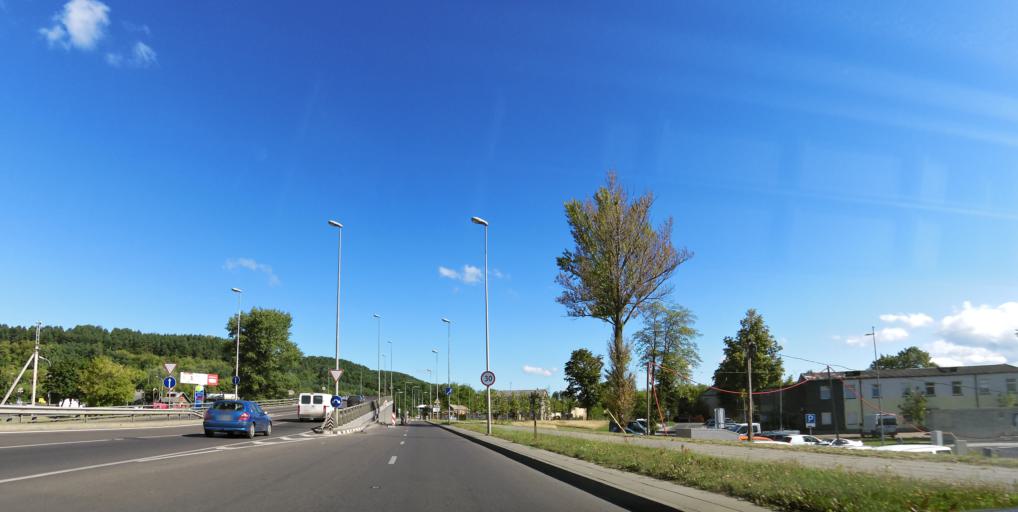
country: LT
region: Vilnius County
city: Seskine
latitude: 54.6999
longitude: 25.2641
